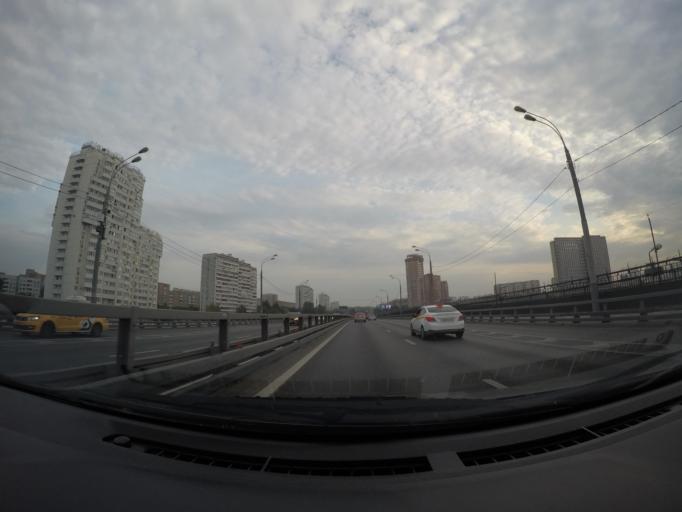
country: RU
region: Moskovskaya
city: Kozhukhovo
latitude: 55.6861
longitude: 37.6651
